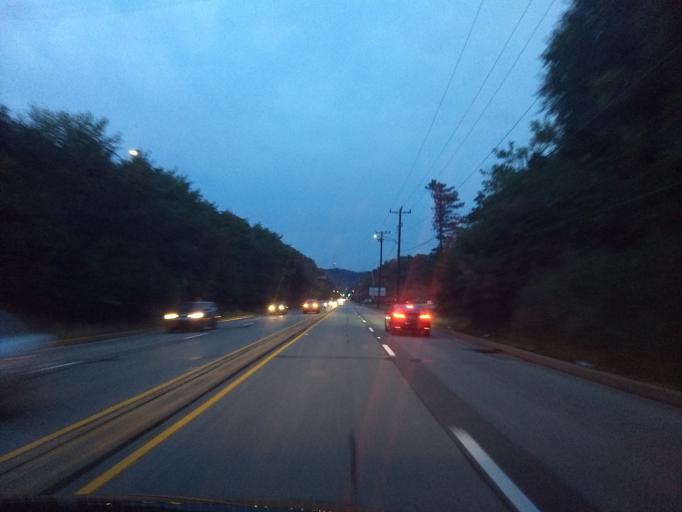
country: US
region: Pennsylvania
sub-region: Allegheny County
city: East Pittsburgh
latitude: 40.3864
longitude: -79.8268
